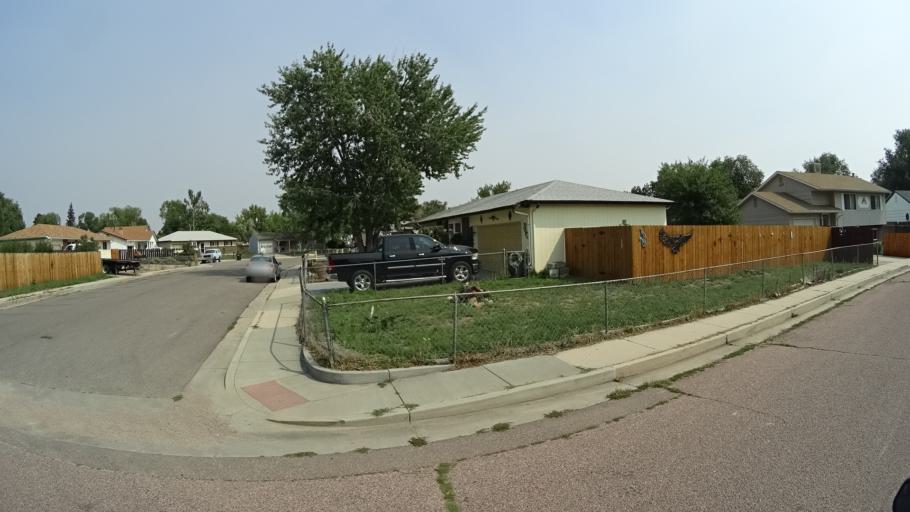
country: US
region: Colorado
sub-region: El Paso County
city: Colorado Springs
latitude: 38.8023
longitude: -104.8101
